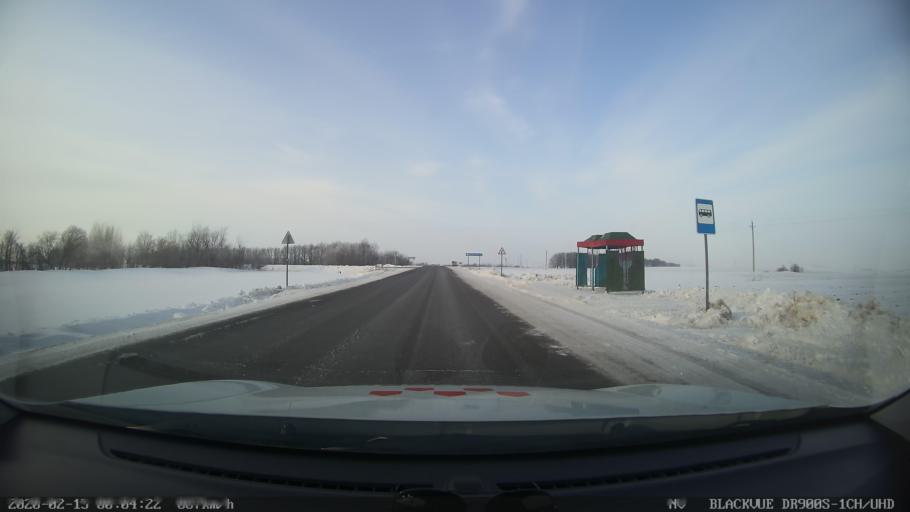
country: RU
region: Tatarstan
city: Kuybyshevskiy Zaton
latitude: 55.3817
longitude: 48.9844
